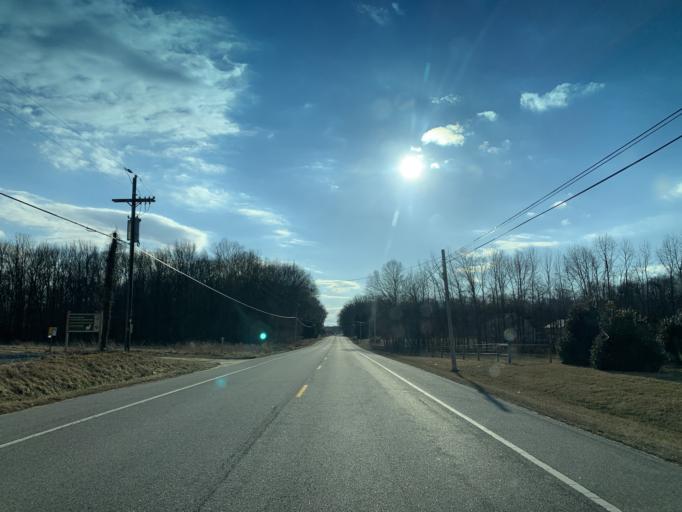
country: US
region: Maryland
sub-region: Queen Anne's County
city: Kingstown
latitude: 39.1693
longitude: -75.9260
